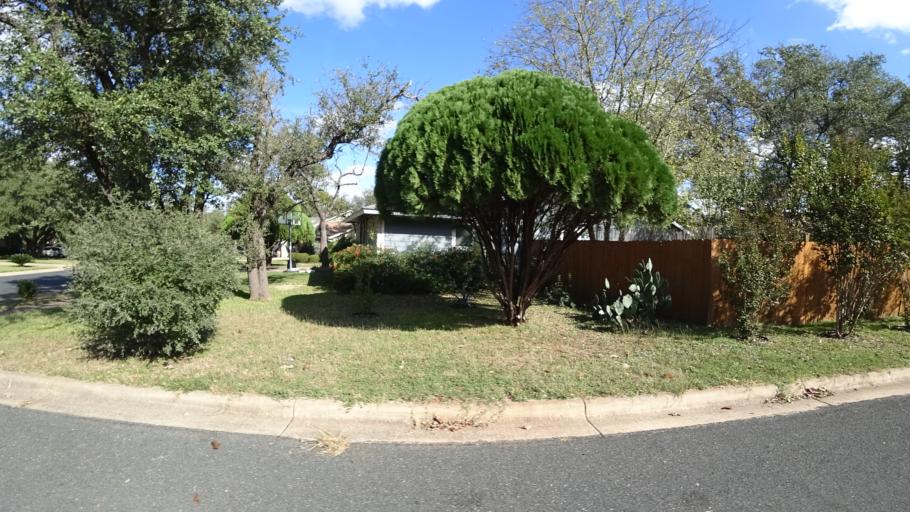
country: US
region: Texas
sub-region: Williamson County
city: Jollyville
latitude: 30.4242
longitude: -97.7276
